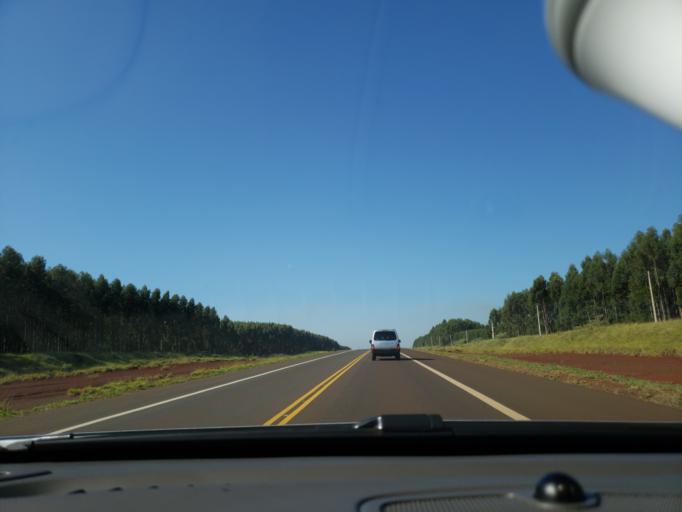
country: AR
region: Misiones
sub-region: Departamento de Capital
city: Posadas
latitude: -27.4653
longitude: -55.9545
